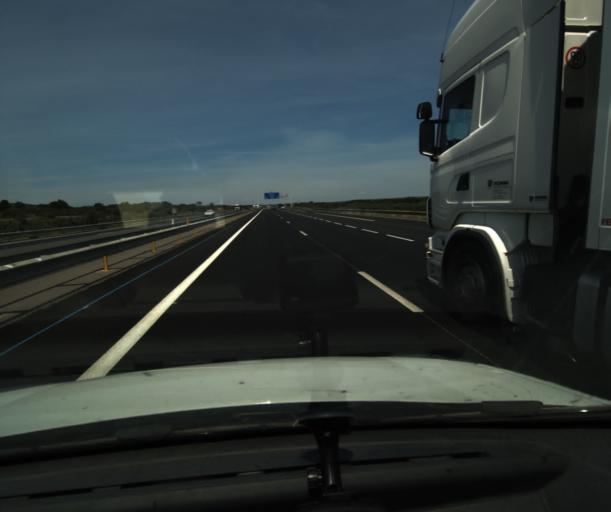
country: FR
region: Languedoc-Roussillon
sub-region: Departement de l'Aude
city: Leucate
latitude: 42.9340
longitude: 2.9694
